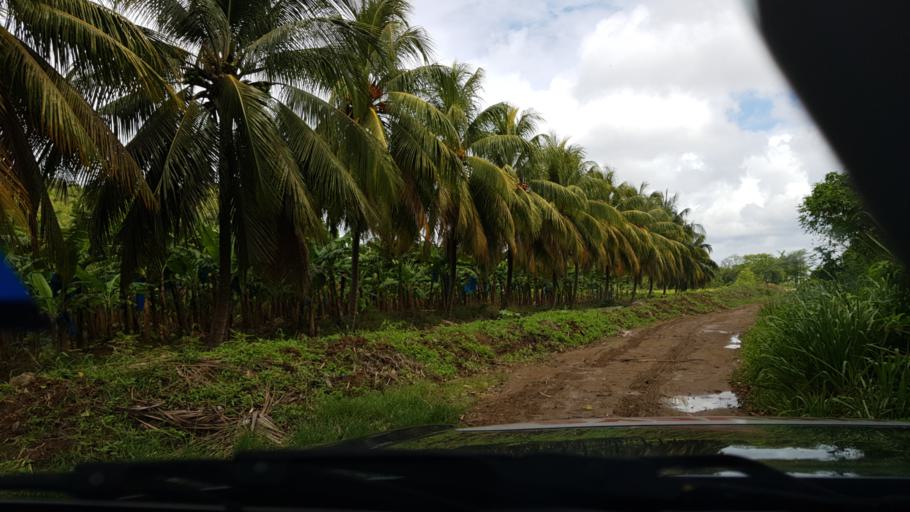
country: LC
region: Anse-la-Raye
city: Anse La Raye
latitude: 13.9545
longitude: -61.0312
